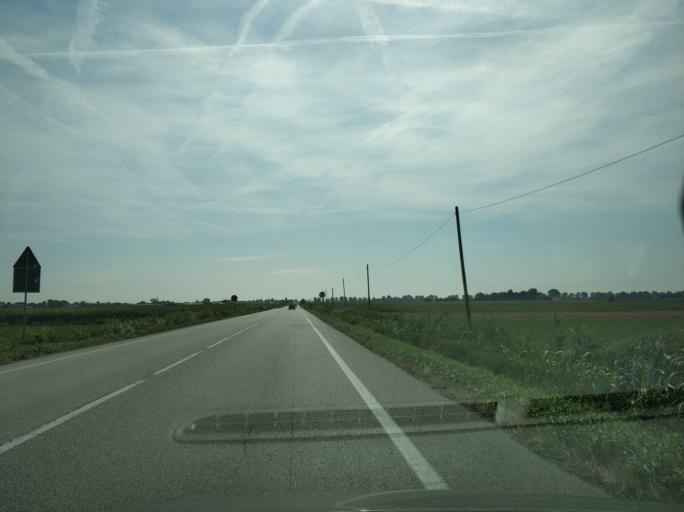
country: IT
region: Veneto
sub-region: Provincia di Padova
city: Candiana
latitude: 45.2134
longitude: 12.0105
